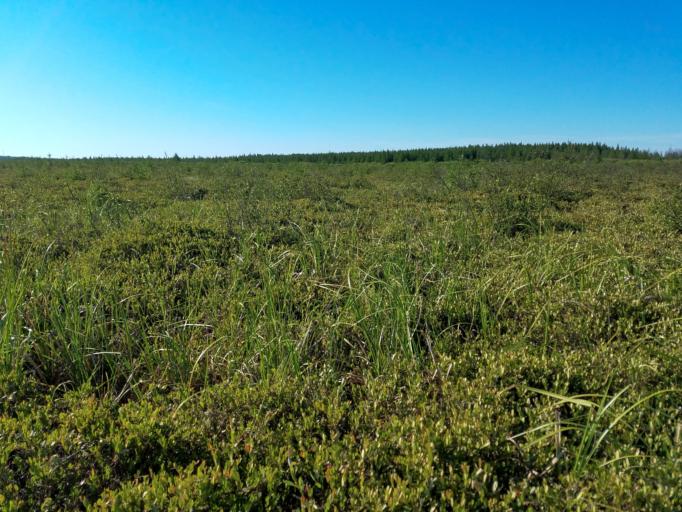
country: US
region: Wisconsin
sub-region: Vilas County
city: Eagle River
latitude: 45.8110
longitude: -89.2168
